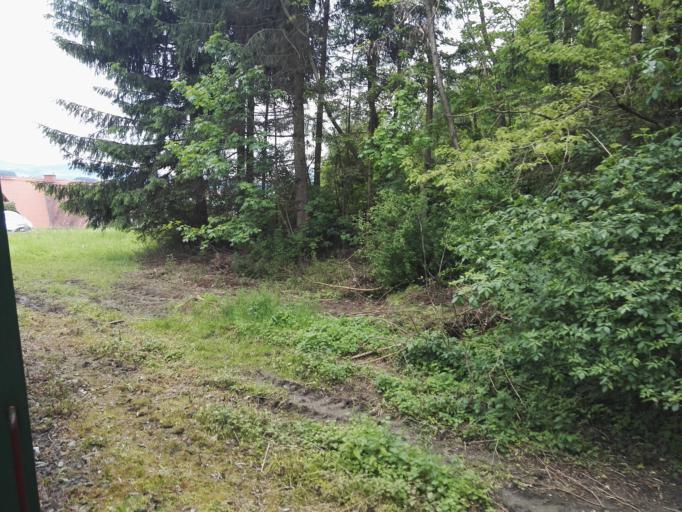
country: AT
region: Styria
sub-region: Politischer Bezirk Weiz
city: Unterfladnitz
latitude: 47.2275
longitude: 15.6723
